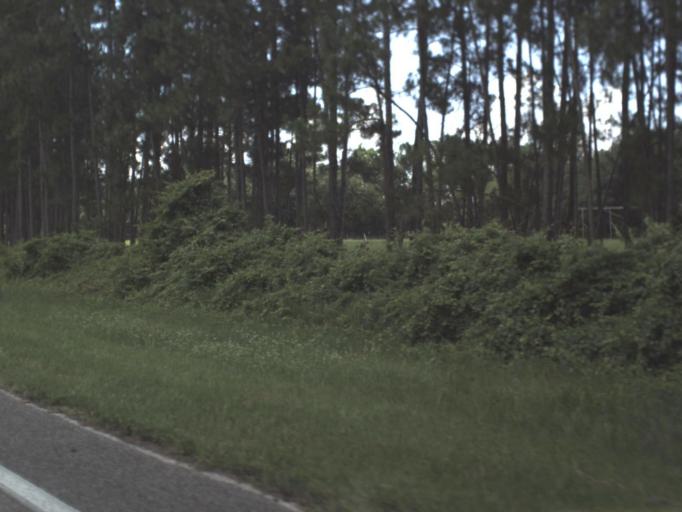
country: US
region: Florida
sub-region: Putnam County
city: East Palatka
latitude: 29.5662
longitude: -81.5457
